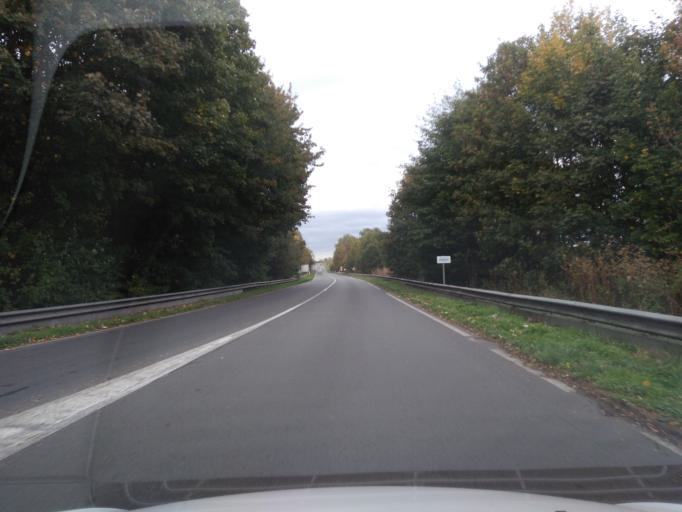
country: FR
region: Nord-Pas-de-Calais
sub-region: Departement du Nord
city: Saultain
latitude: 50.3491
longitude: 3.5727
